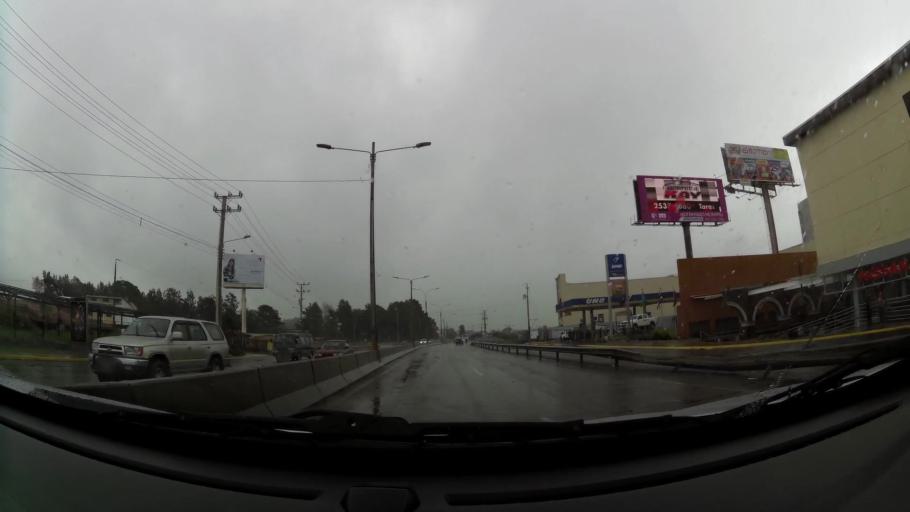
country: CR
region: Cartago
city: Cartago
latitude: 9.8680
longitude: -83.9427
